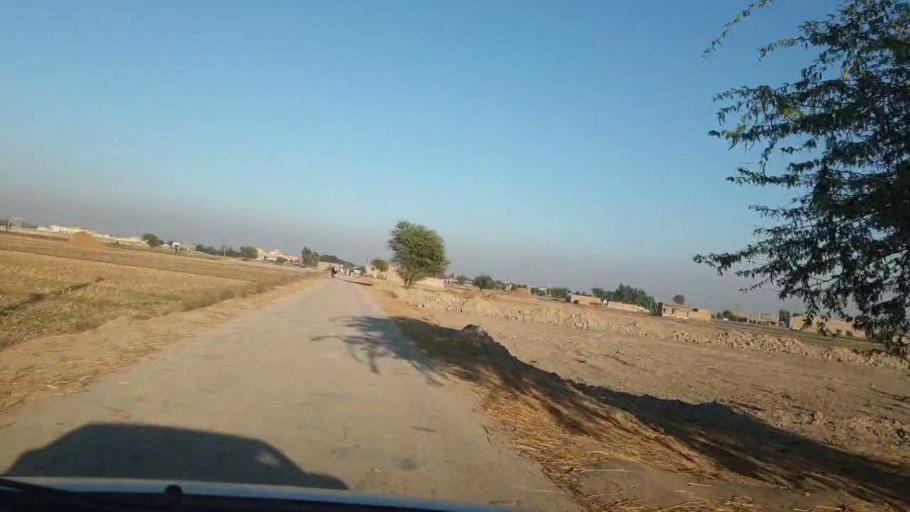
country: PK
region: Sindh
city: Khairpur Nathan Shah
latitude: 27.0736
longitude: 67.7223
